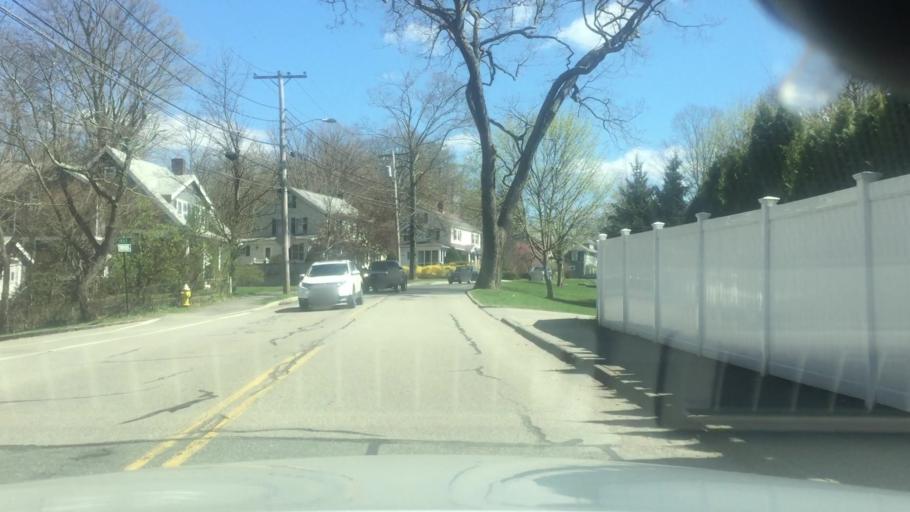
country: US
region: Massachusetts
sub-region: Norfolk County
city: Needham
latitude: 42.2832
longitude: -71.2414
